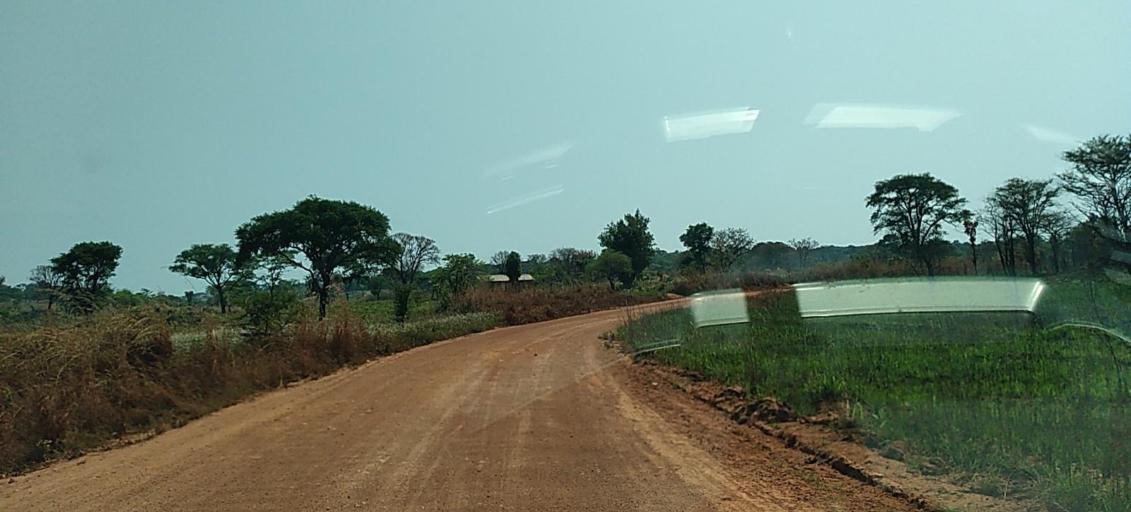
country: ZM
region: North-Western
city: Kansanshi
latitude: -12.0039
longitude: 26.5563
